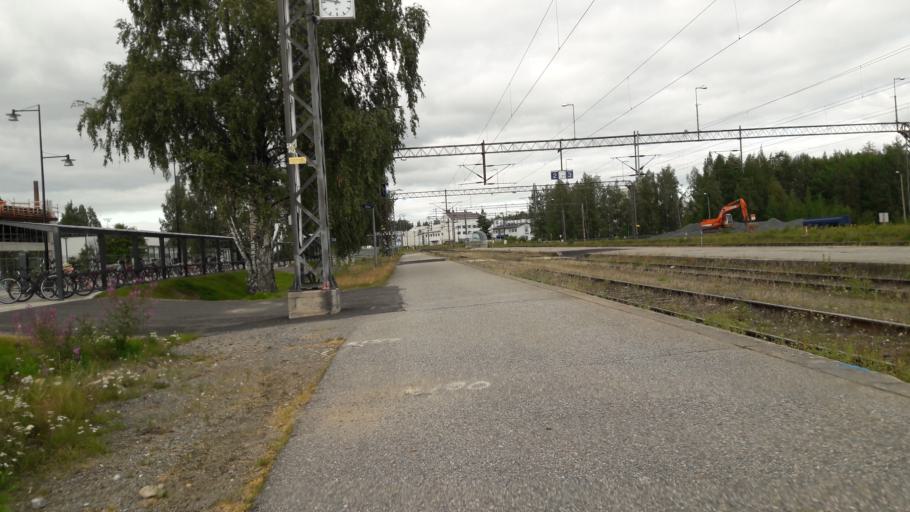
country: FI
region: North Karelia
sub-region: Joensuu
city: Joensuu
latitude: 62.6006
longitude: 29.7773
